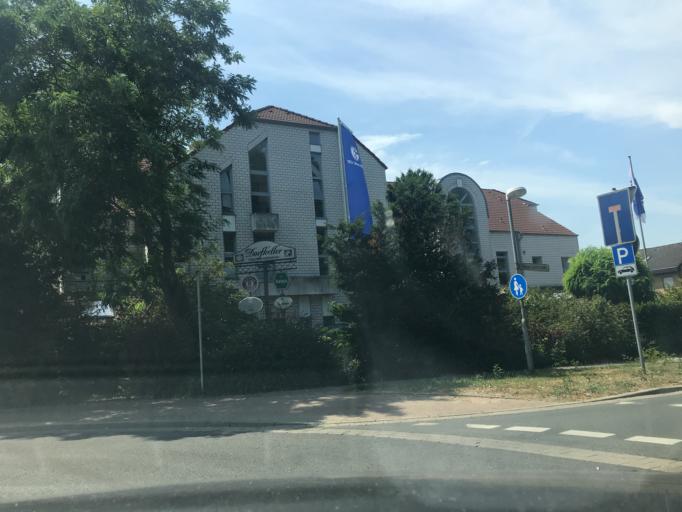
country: DE
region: North Rhine-Westphalia
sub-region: Regierungsbezirk Dusseldorf
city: Wesel
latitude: 51.6851
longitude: 6.5761
